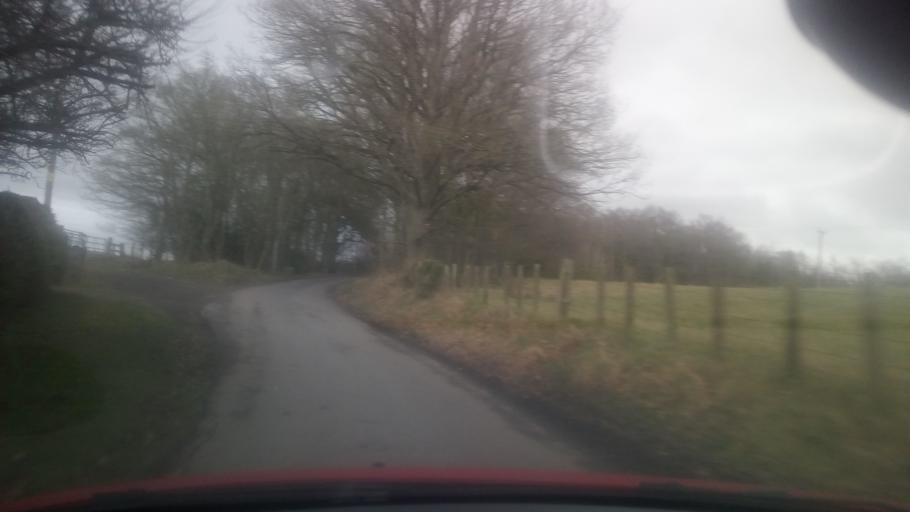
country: GB
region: Scotland
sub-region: The Scottish Borders
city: Jedburgh
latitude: 55.4698
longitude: -2.5362
